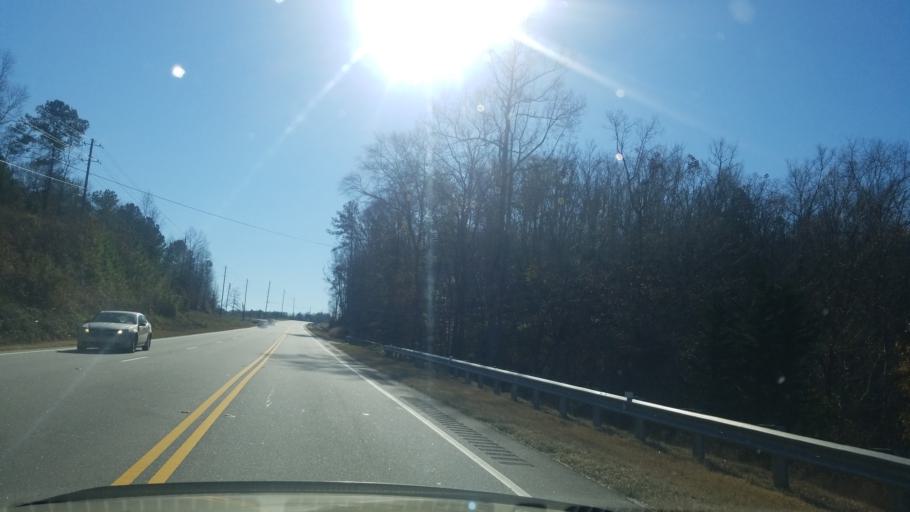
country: US
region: Georgia
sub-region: Troup County
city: West Point
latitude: 32.8595
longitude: -85.1340
